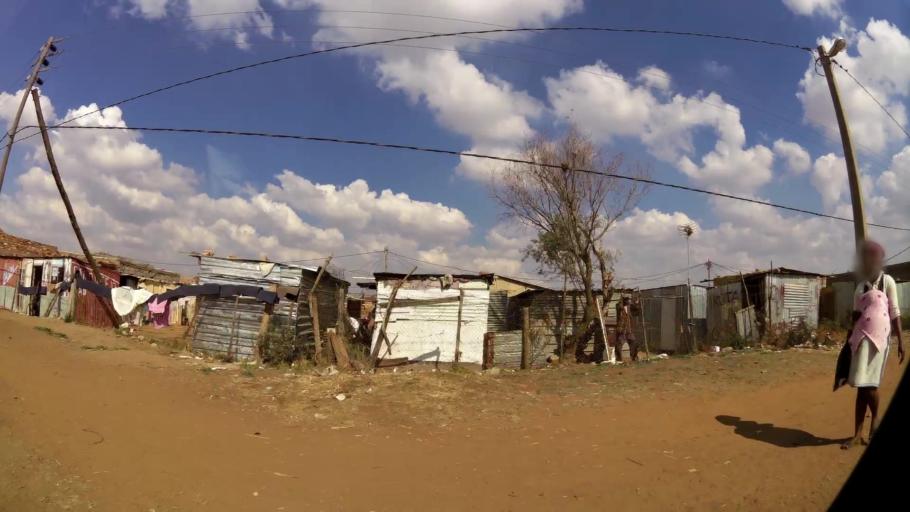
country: ZA
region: Gauteng
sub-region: City of Johannesburg Metropolitan Municipality
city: Roodepoort
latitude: -26.1899
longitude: 27.8708
